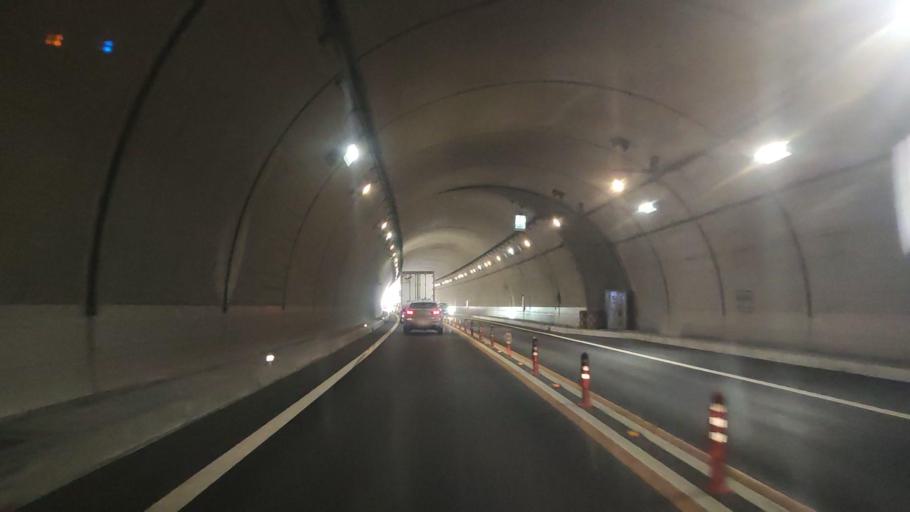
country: JP
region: Fukuoka
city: Kanda
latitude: 33.7753
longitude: 130.9695
